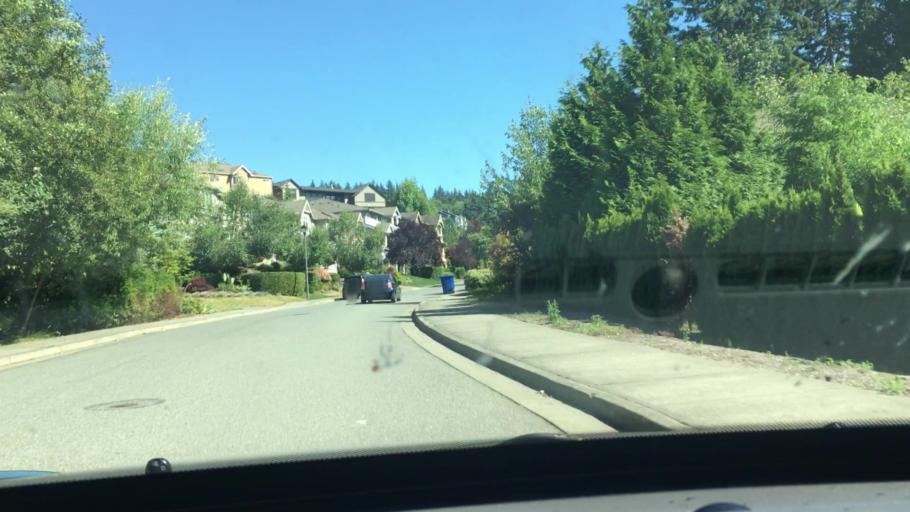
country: US
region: Washington
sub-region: King County
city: Newcastle
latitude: 47.5396
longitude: -122.1184
